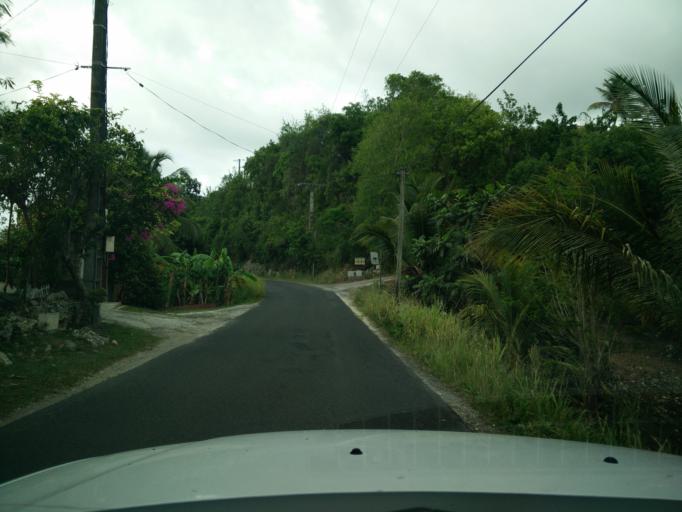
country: GP
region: Guadeloupe
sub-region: Guadeloupe
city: Le Gosier
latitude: 16.2381
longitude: -61.4502
